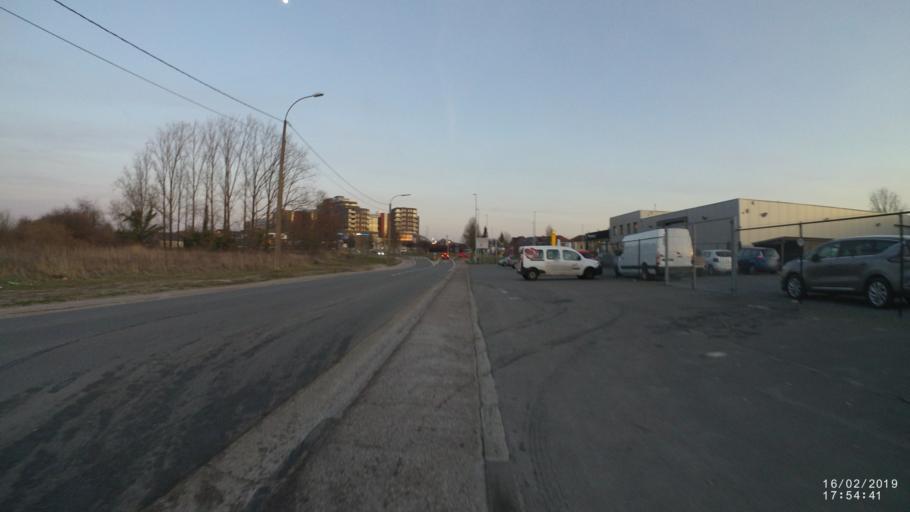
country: BE
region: Flanders
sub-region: Provincie Limburg
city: Sint-Truiden
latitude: 50.8147
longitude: 5.1602
